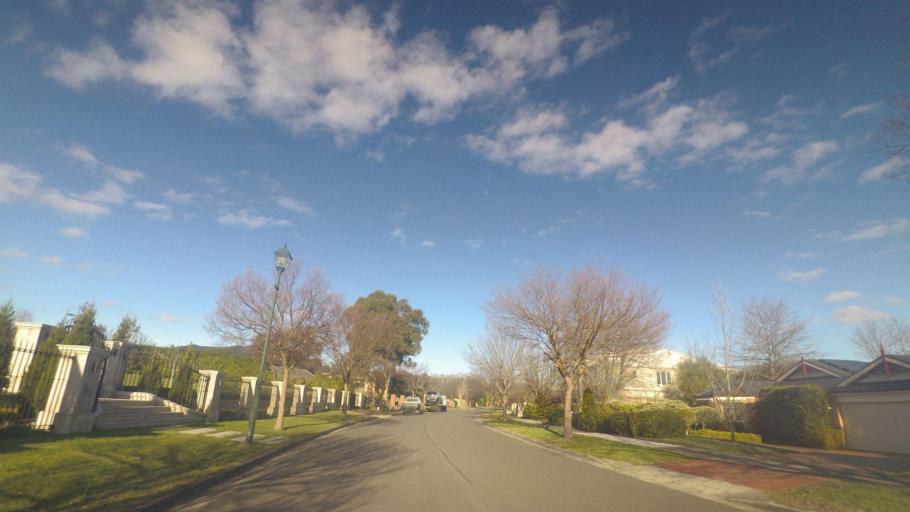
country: AU
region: Victoria
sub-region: Yarra Ranges
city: Lysterfield
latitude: -37.9123
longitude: 145.2867
